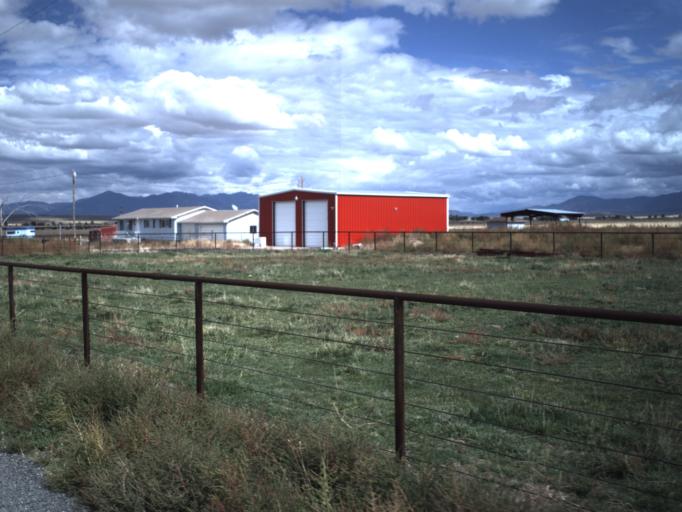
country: US
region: Utah
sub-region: Millard County
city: Fillmore
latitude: 39.0239
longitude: -112.4100
